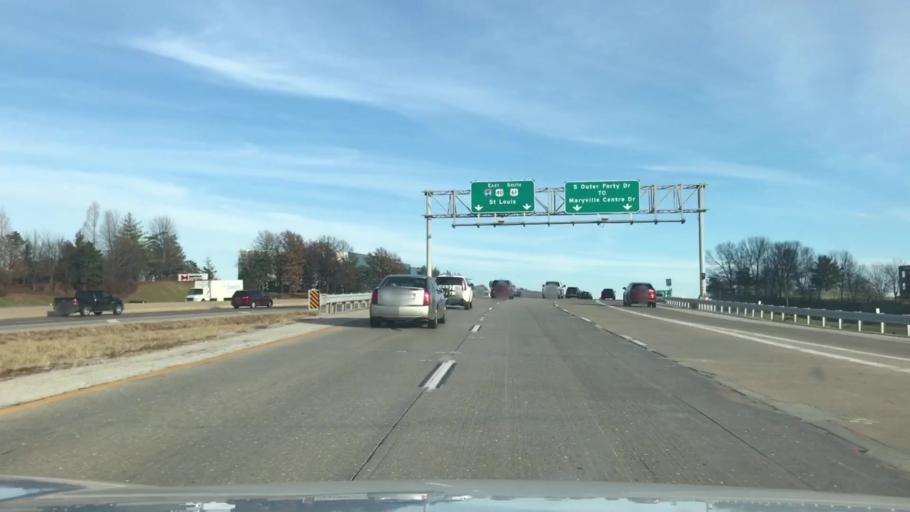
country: US
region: Missouri
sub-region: Saint Louis County
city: Manchester
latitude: 38.6413
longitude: -90.5081
